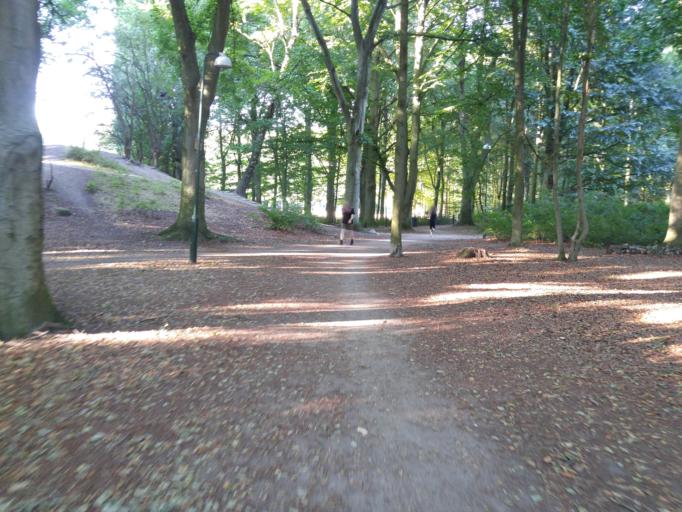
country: SE
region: Skane
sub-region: Malmo
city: Malmoe
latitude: 55.5886
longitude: 12.9887
